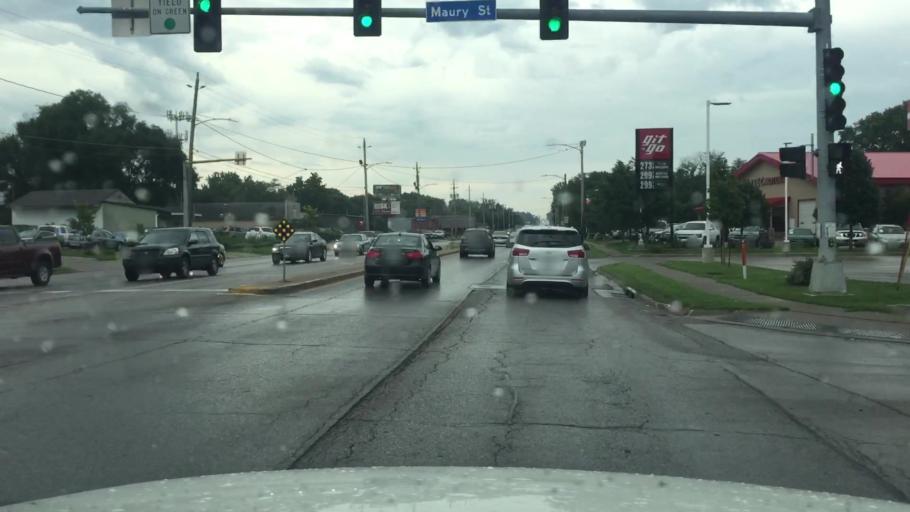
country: US
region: Iowa
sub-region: Polk County
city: Des Moines
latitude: 41.5812
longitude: -93.5970
